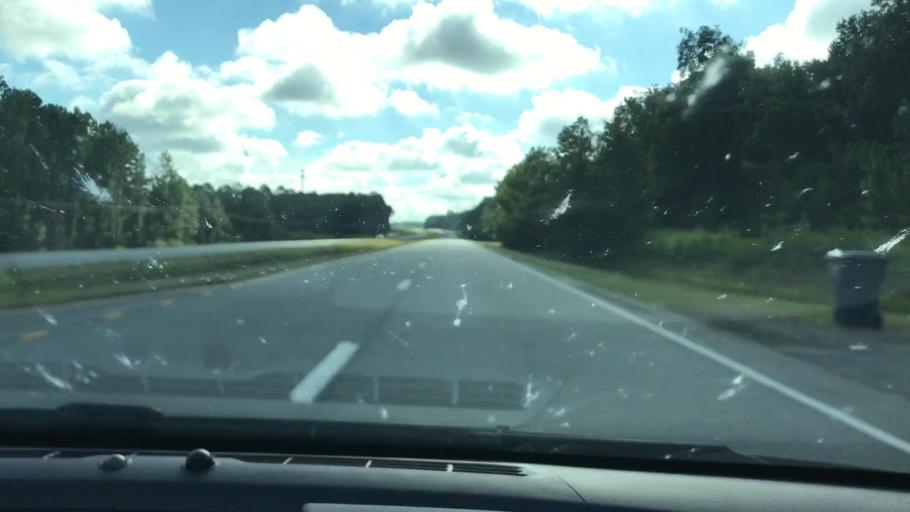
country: US
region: Georgia
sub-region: Worth County
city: Sylvester
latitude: 31.5522
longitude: -83.9475
